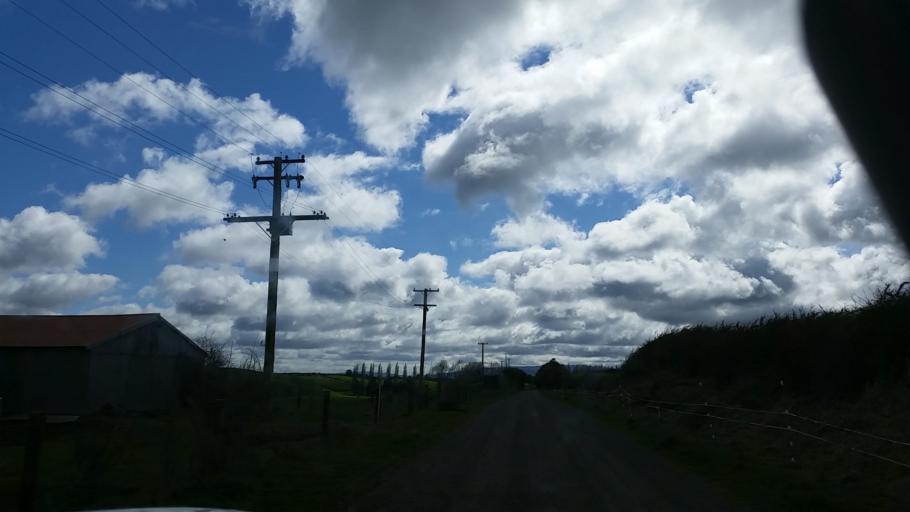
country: NZ
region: Bay of Plenty
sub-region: Whakatane District
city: Murupara
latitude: -38.3104
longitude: 176.4689
